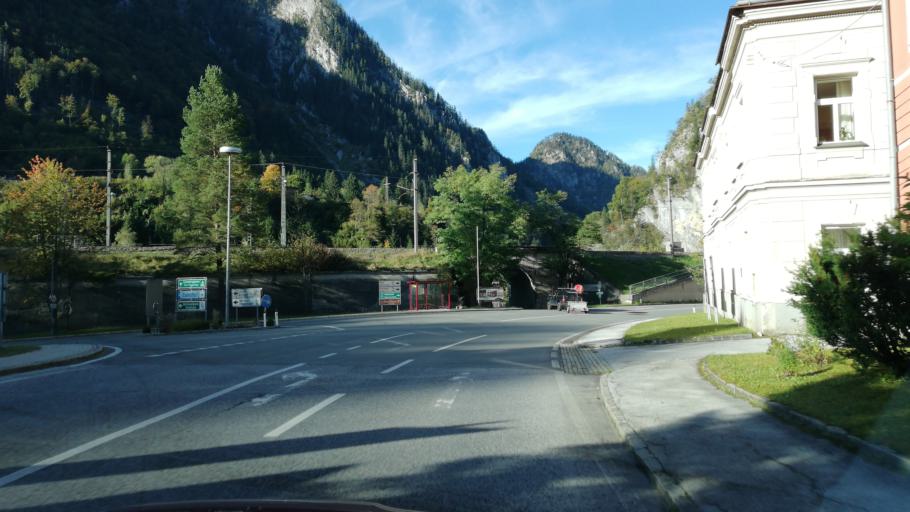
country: AT
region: Styria
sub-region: Politischer Bezirk Leoben
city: Hieflau
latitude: 47.6073
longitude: 14.7437
